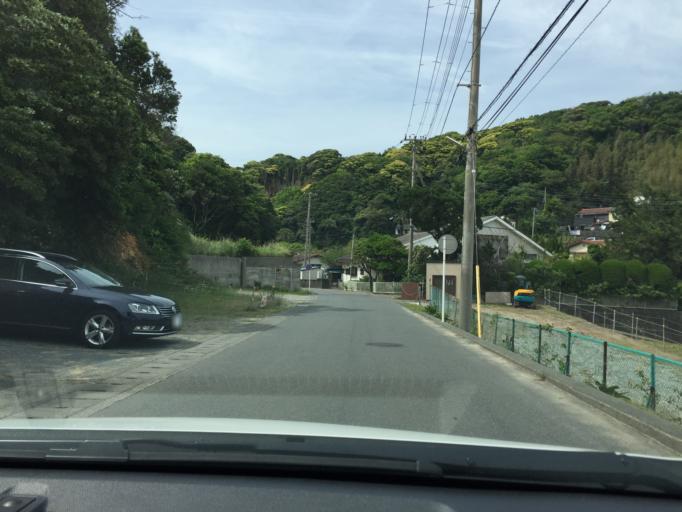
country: JP
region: Shizuoka
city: Shimoda
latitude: 34.6751
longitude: 138.9712
